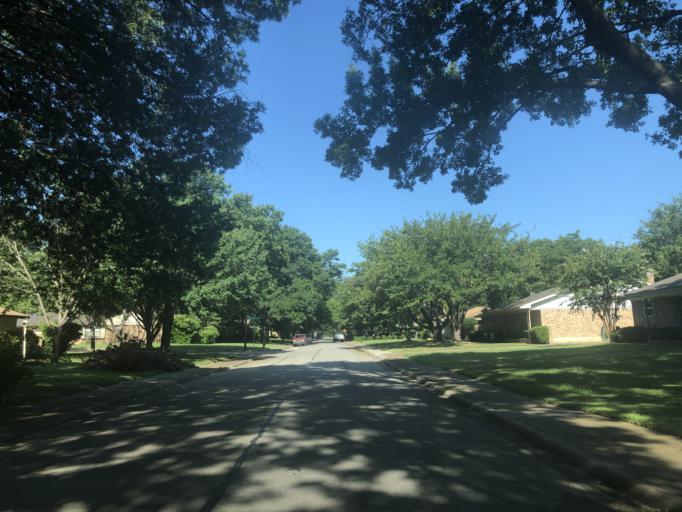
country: US
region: Texas
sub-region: Dallas County
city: Grand Prairie
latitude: 32.7529
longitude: -97.0183
